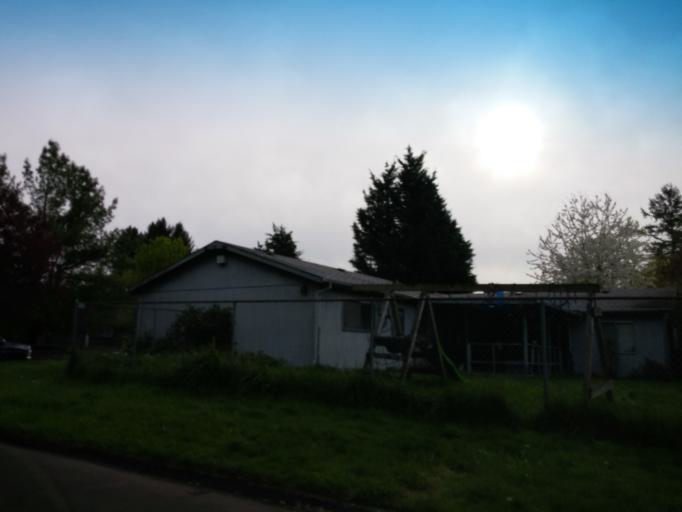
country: US
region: Oregon
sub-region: Washington County
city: Cedar Mill
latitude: 45.5120
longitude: -122.8176
